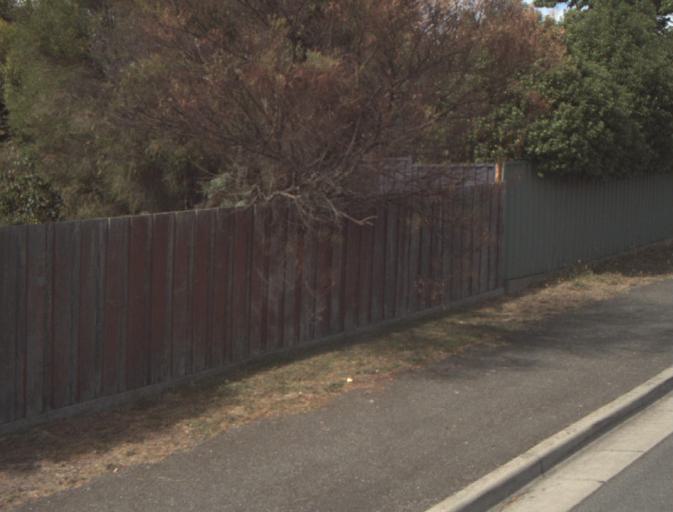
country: AU
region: Tasmania
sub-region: Launceston
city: Summerhill
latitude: -41.4675
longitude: 147.1285
